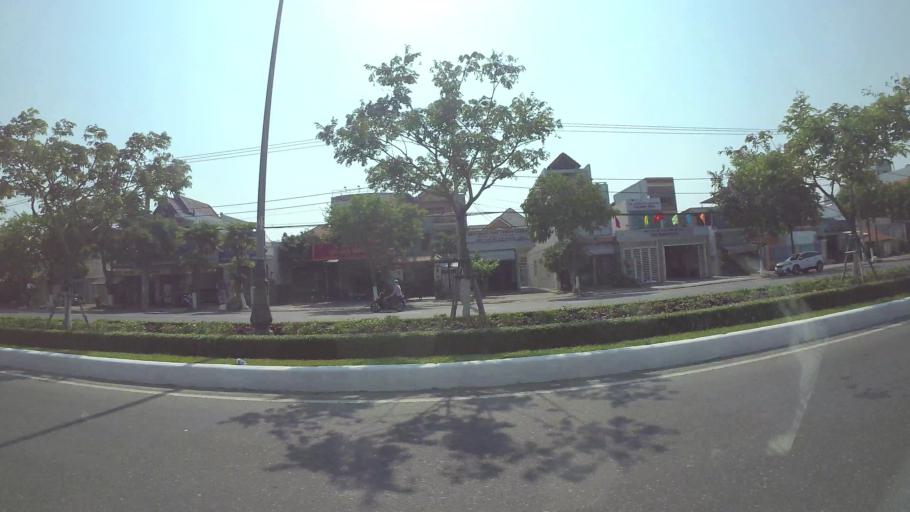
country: VN
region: Da Nang
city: Ngu Hanh Son
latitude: 16.0298
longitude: 108.2474
